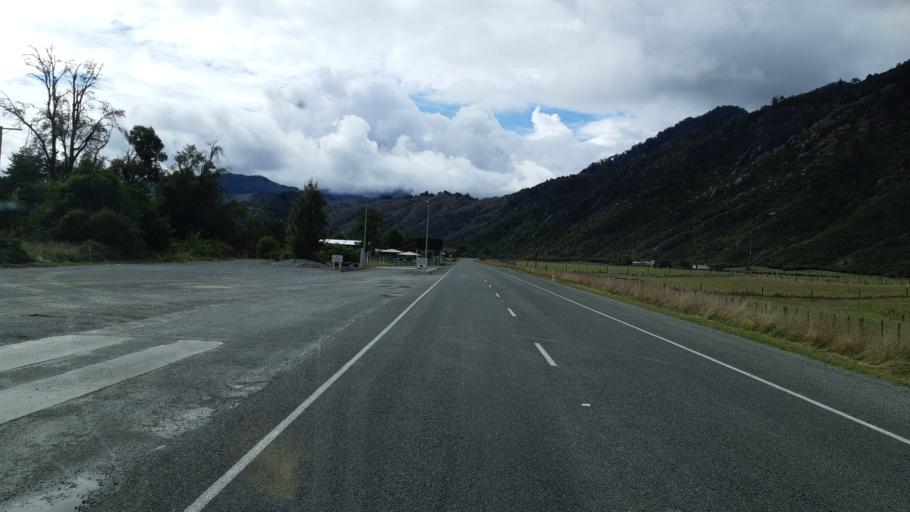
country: NZ
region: West Coast
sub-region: Buller District
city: Westport
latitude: -41.7964
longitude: 172.3481
